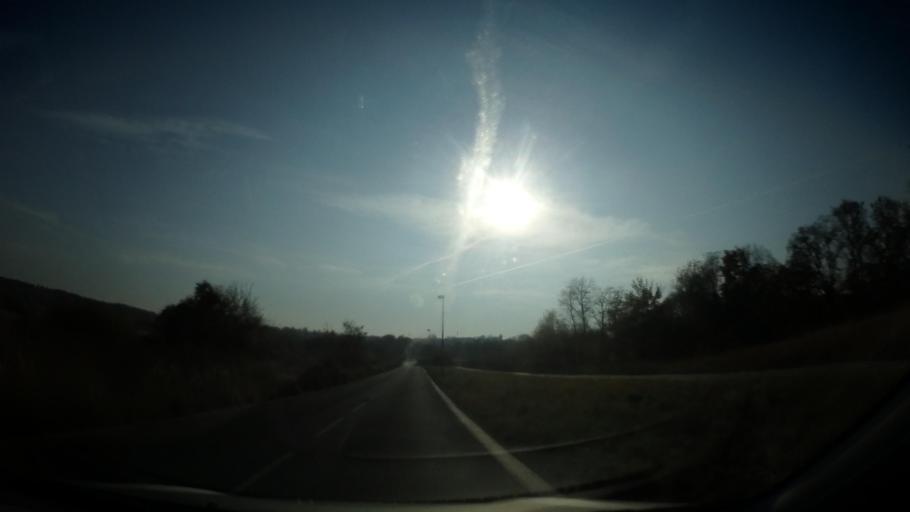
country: CZ
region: Praha
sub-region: Praha 14
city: Dolni Pocernice
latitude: 50.0918
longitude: 14.5842
